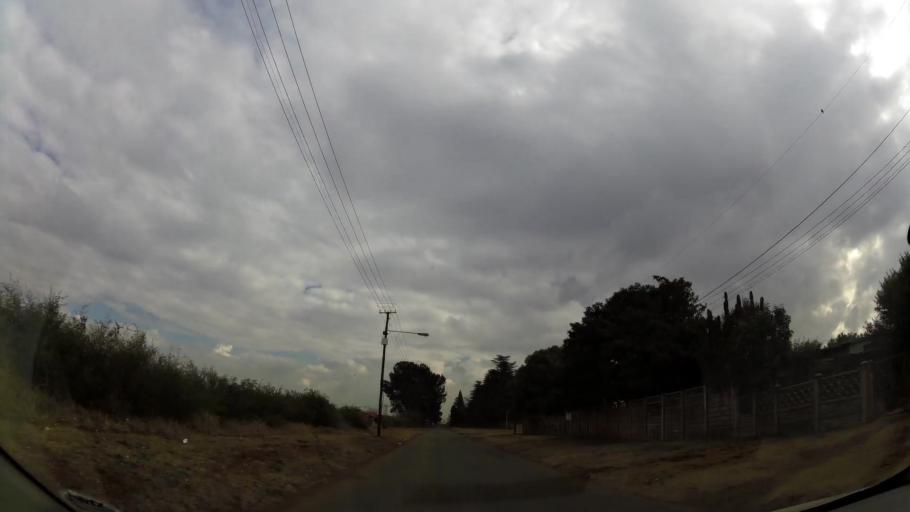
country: ZA
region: Gauteng
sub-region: Sedibeng District Municipality
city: Meyerton
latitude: -26.5934
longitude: 27.9947
